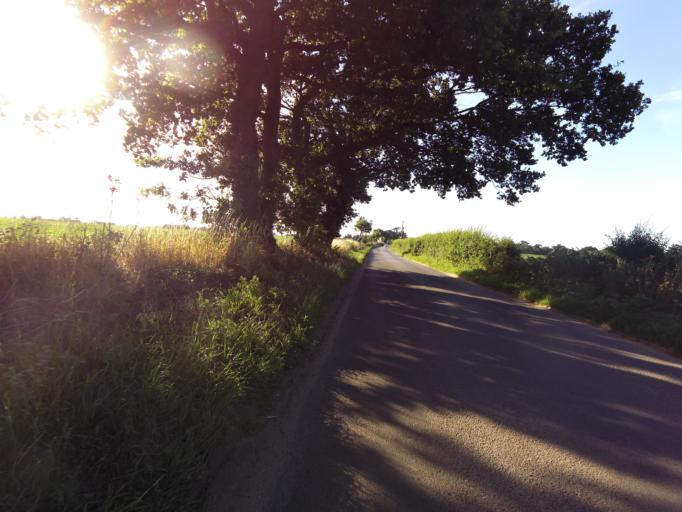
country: GB
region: England
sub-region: Suffolk
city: Kesgrave
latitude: 52.0136
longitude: 1.2261
